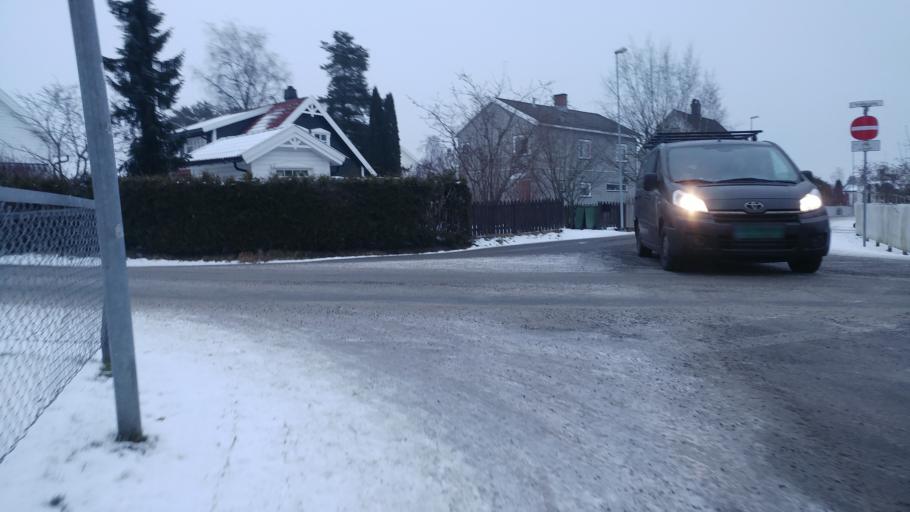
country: NO
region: Akershus
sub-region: Skedsmo
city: Lillestrom
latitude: 59.9628
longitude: 11.0350
